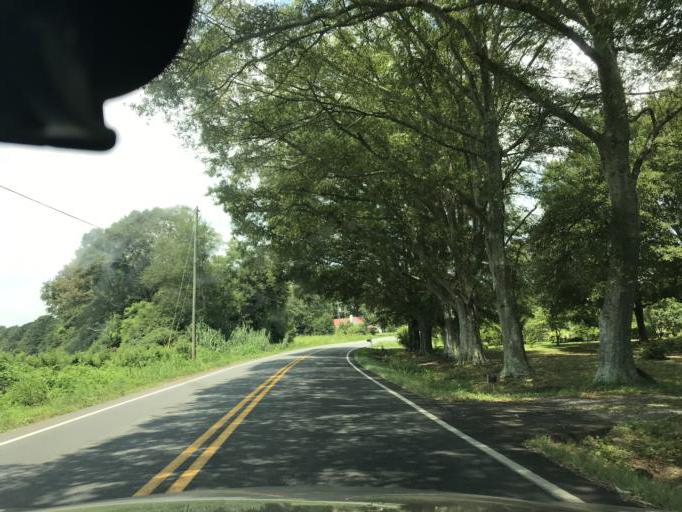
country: US
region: Georgia
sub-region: Dawson County
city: Dawsonville
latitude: 34.3353
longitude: -84.1327
